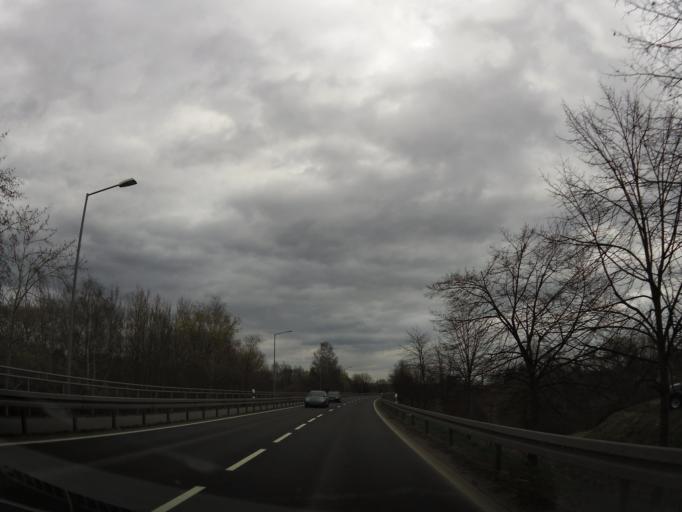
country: DE
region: Thuringia
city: Ilmenau
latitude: 50.6920
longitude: 10.9254
